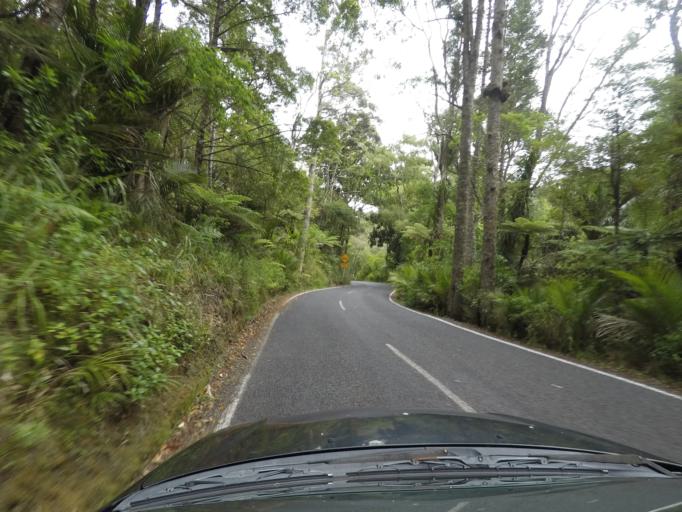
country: NZ
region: Auckland
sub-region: Auckland
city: Titirangi
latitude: -36.9491
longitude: 174.6584
